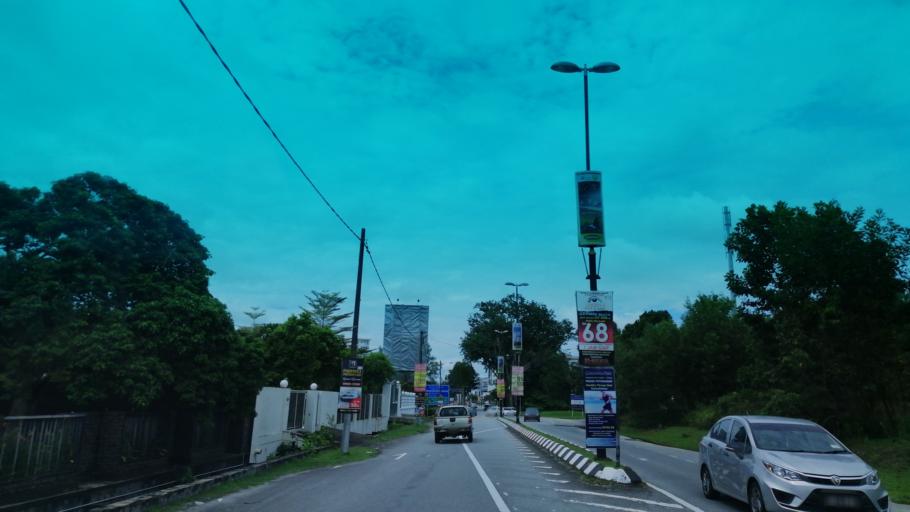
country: MY
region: Perak
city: Taiping
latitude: 4.8632
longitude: 100.7338
